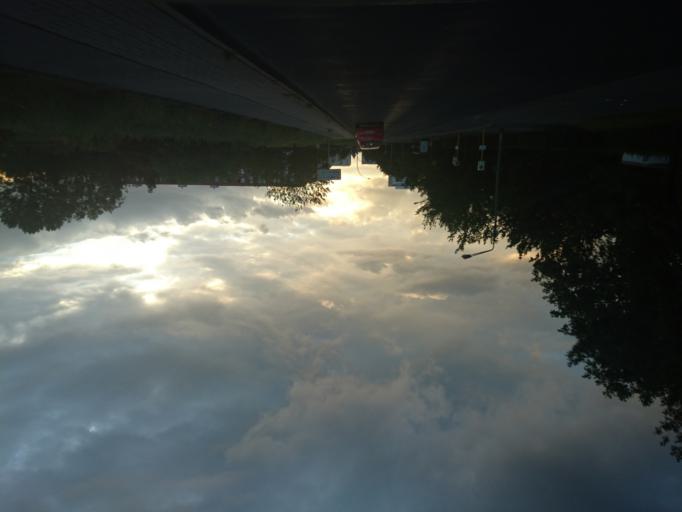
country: DE
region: Berlin
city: Marzahn
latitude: 52.5400
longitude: 13.5789
